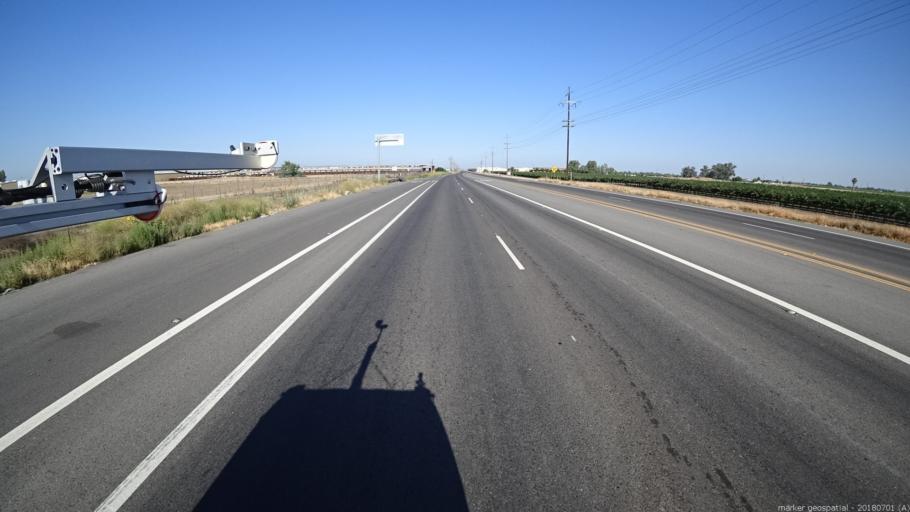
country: US
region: California
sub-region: Madera County
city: Parkwood
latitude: 36.9236
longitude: -120.0287
